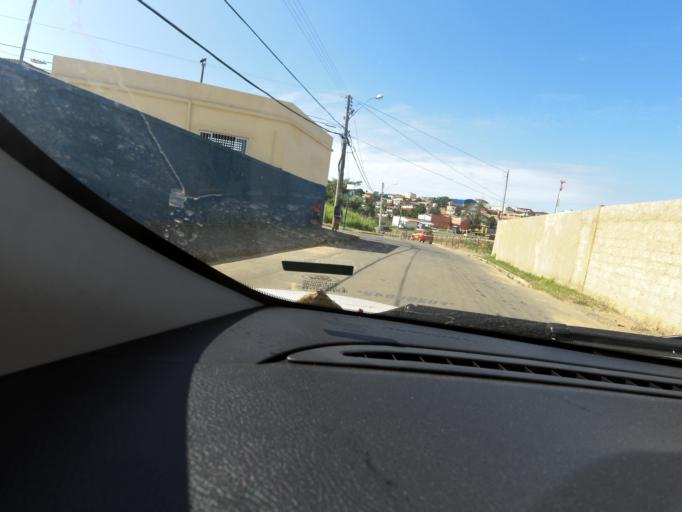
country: BR
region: Espirito Santo
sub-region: Guarapari
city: Guarapari
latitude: -20.6460
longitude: -40.5158
